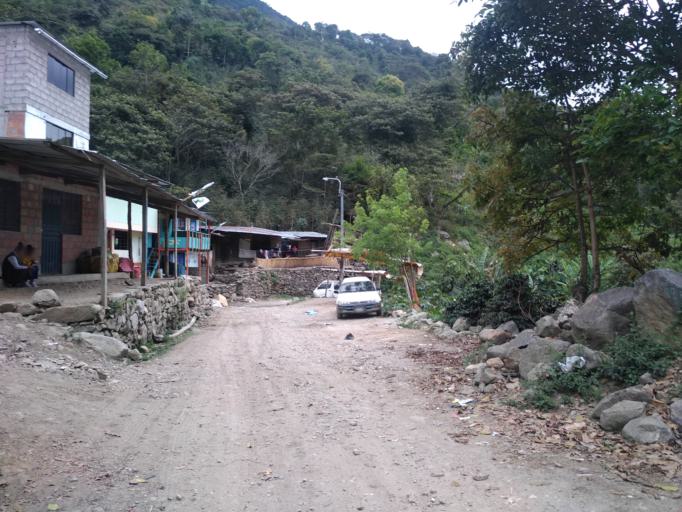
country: PE
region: Cusco
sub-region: Provincia de La Convencion
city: Santa Teresa
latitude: -13.2280
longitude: -72.6289
